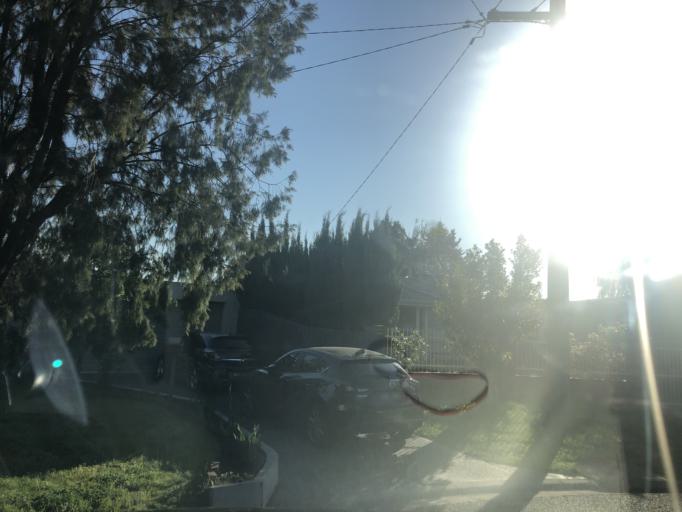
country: AU
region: Victoria
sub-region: Casey
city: Hampton Park
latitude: -38.0388
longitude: 145.2629
